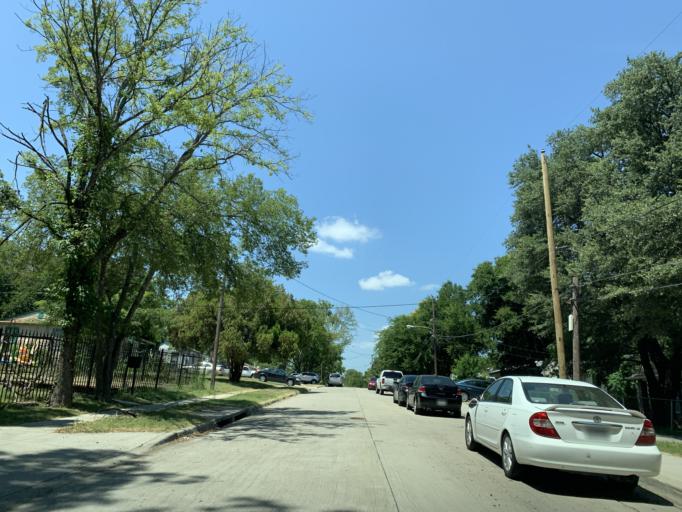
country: US
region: Texas
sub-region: Dallas County
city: Hutchins
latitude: 32.6874
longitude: -96.7729
